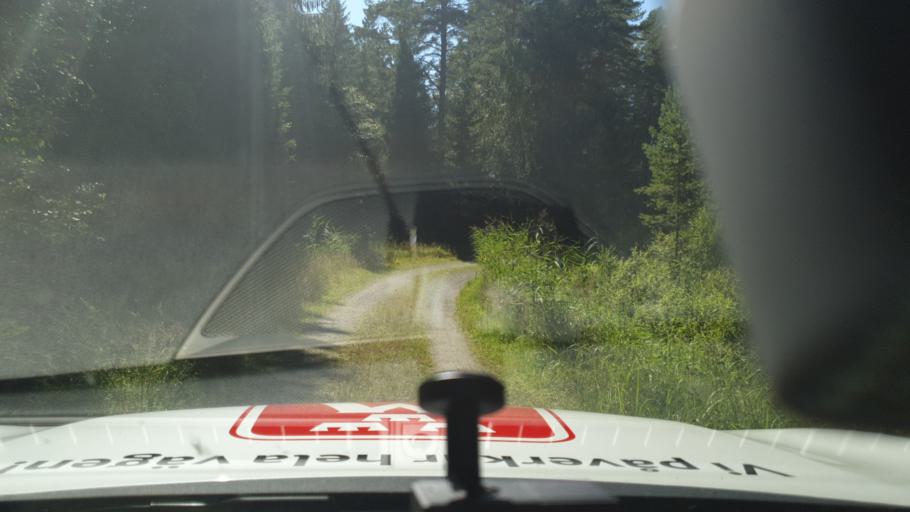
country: SE
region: Vaermland
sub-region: Saffle Kommun
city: Saeffle
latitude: 58.9971
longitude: 13.1839
